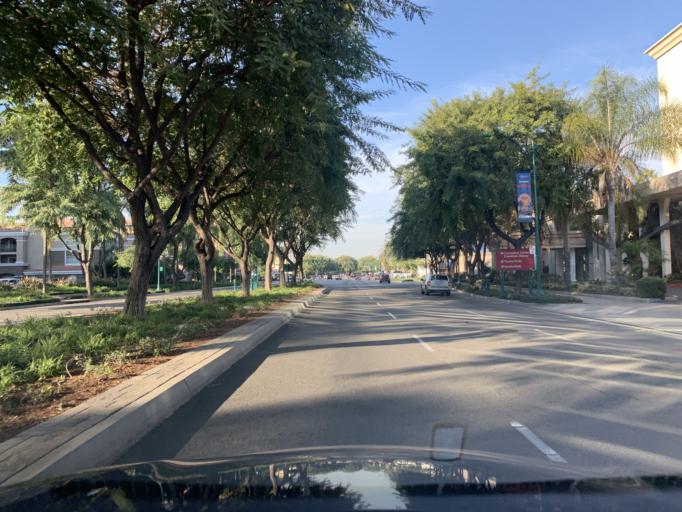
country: US
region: California
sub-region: Orange County
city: Anaheim
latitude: 33.8014
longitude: -117.9152
